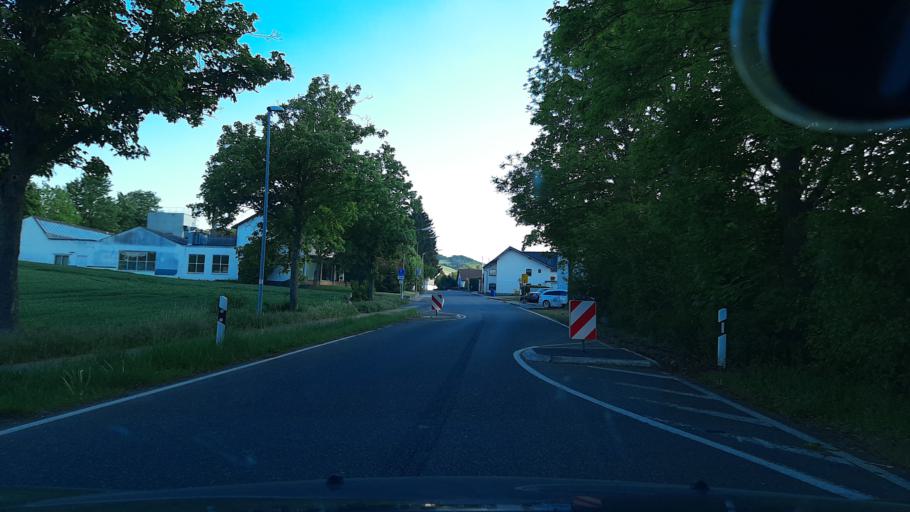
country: DE
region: North Rhine-Westphalia
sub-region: Regierungsbezirk Koln
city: Mechernich
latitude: 50.5731
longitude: 6.6709
